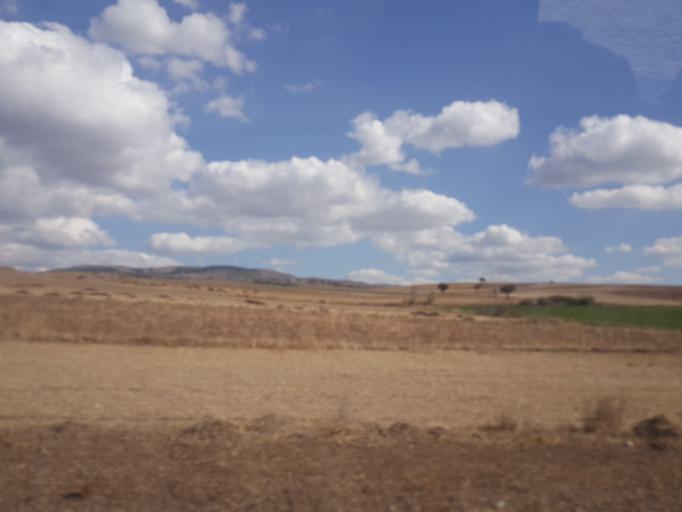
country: TR
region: Tokat
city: Camlibel
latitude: 40.1984
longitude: 36.4664
